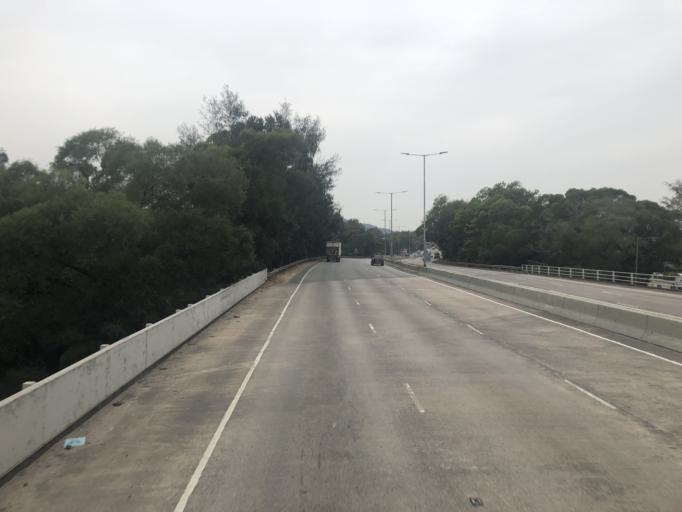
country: CN
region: Guangdong
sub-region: Shenzhen
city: Shenzhen
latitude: 22.5021
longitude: 114.1165
